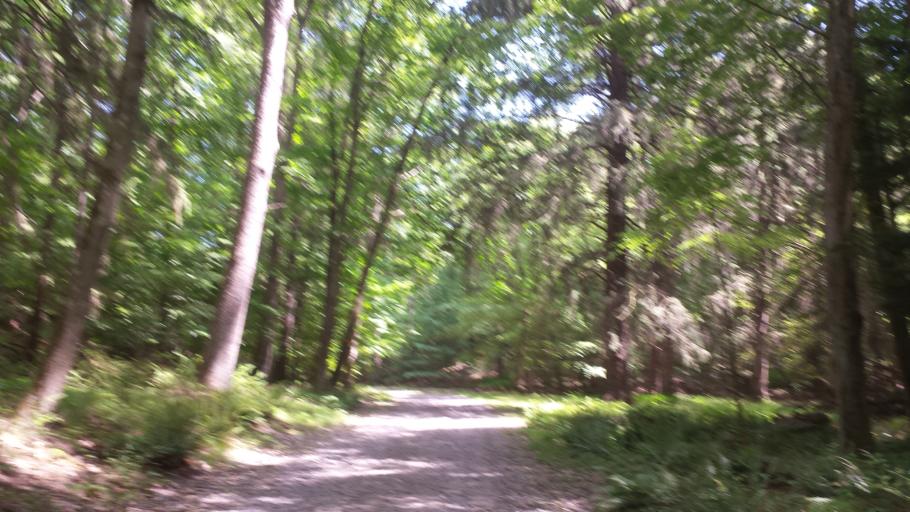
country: US
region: New York
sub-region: Putnam County
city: Peach Lake
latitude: 41.3155
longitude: -73.5711
